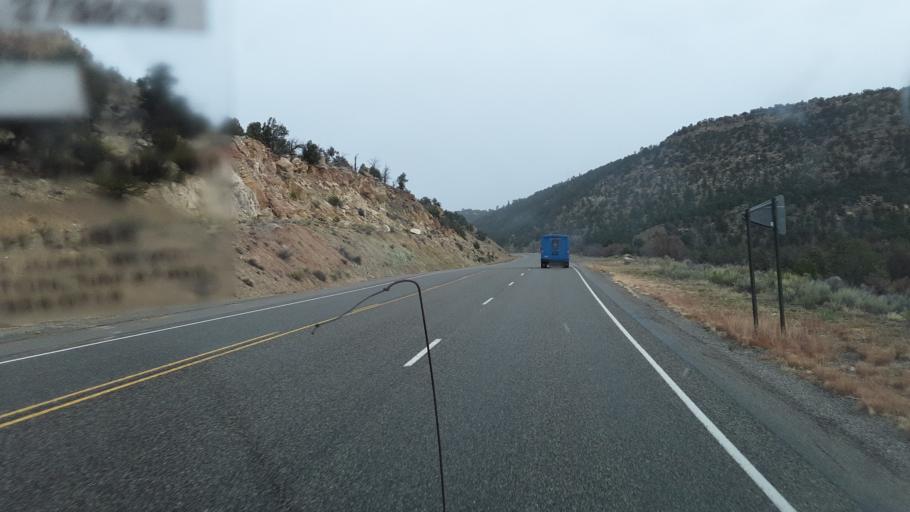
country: US
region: New Mexico
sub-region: Rio Arriba County
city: Tierra Amarilla
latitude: 36.4108
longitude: -106.4854
